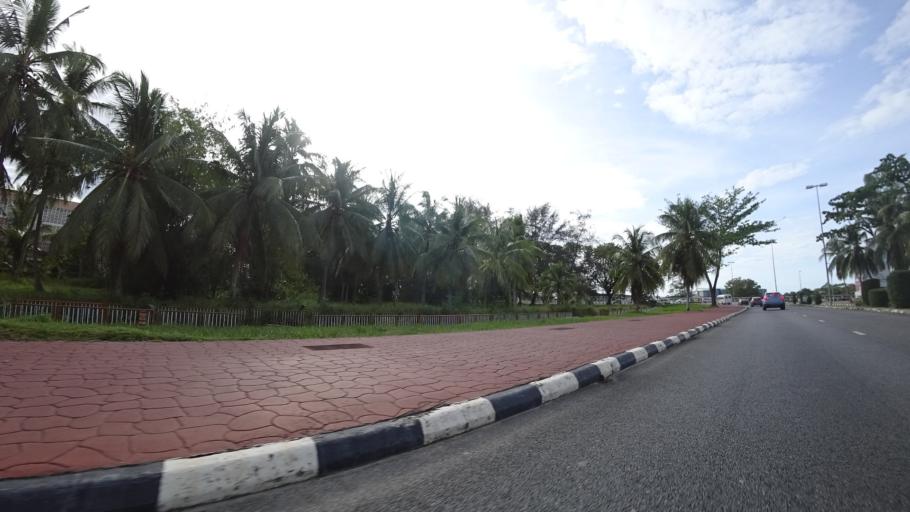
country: BN
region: Brunei and Muara
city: Bandar Seri Begawan
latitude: 4.9282
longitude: 114.9405
